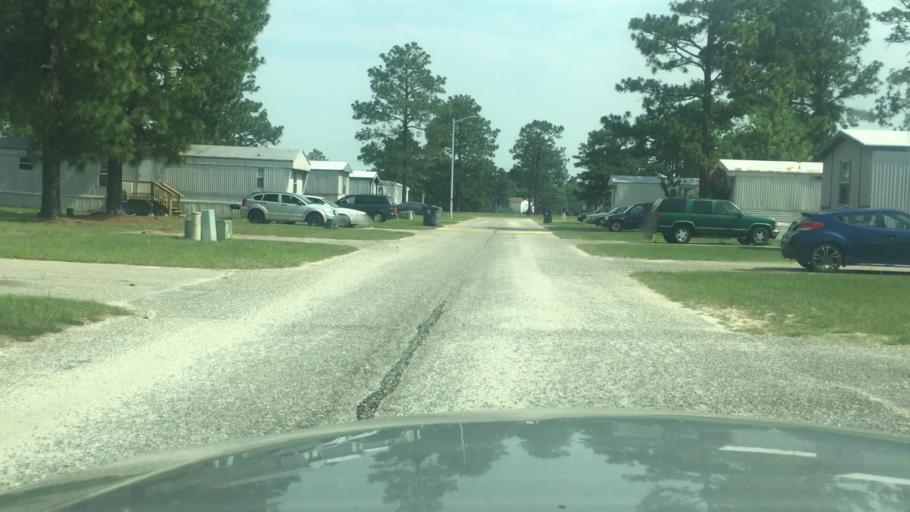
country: US
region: North Carolina
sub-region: Cumberland County
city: Hope Mills
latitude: 34.9984
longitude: -78.9510
